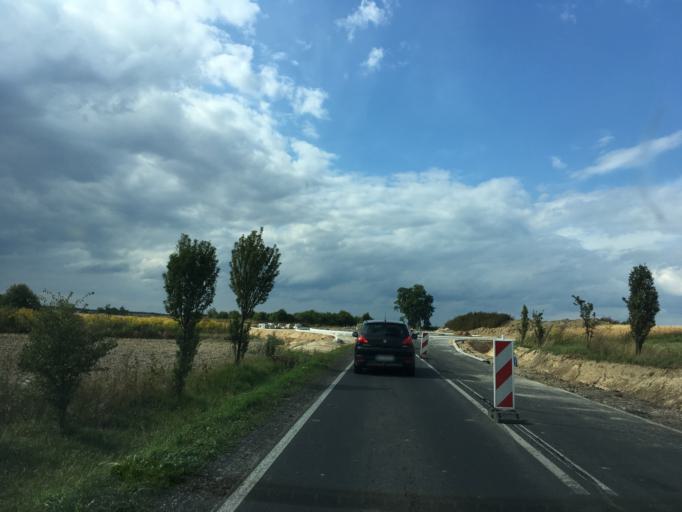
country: PL
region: Lesser Poland Voivodeship
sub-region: Powiat krakowski
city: Skala
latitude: 50.2393
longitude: 19.8390
